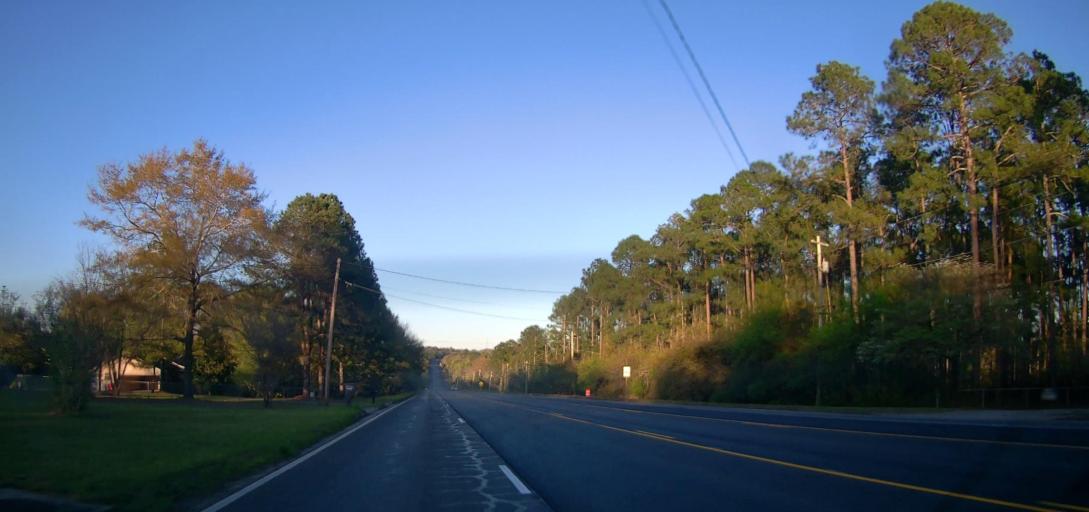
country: US
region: Georgia
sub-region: Bibb County
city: Macon
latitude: 32.8435
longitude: -83.5453
